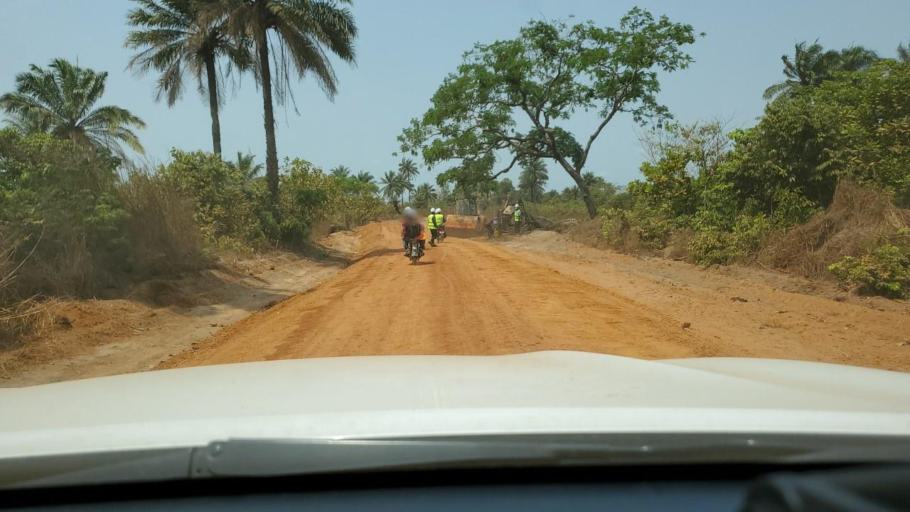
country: GN
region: Boke
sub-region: Boffa
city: Boffa
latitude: 10.0602
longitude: -13.8681
